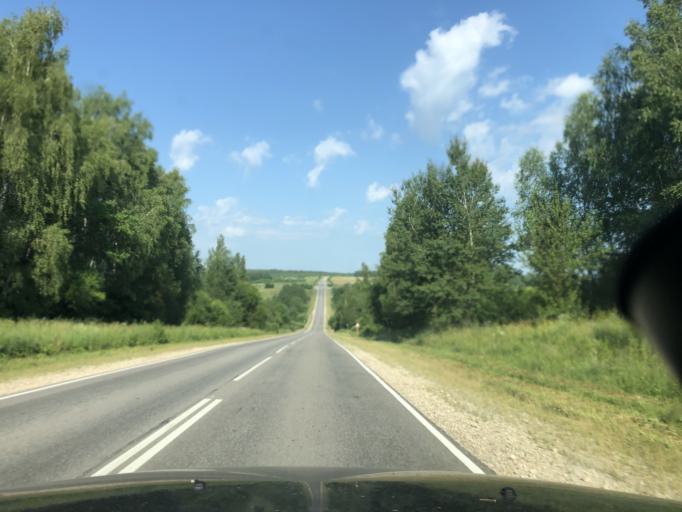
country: RU
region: Tula
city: Dubna
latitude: 54.1292
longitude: 37.0511
